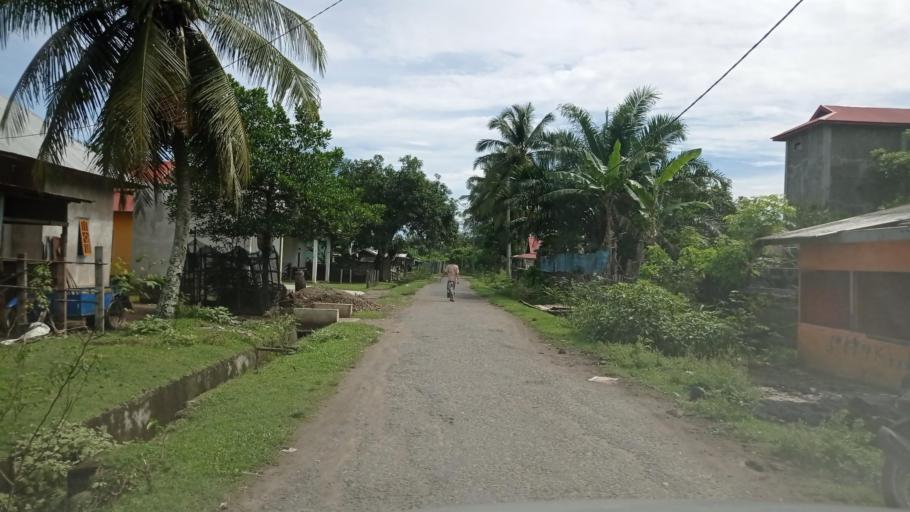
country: ID
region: Bengkulu
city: Ipuh
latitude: -2.5851
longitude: 101.1128
